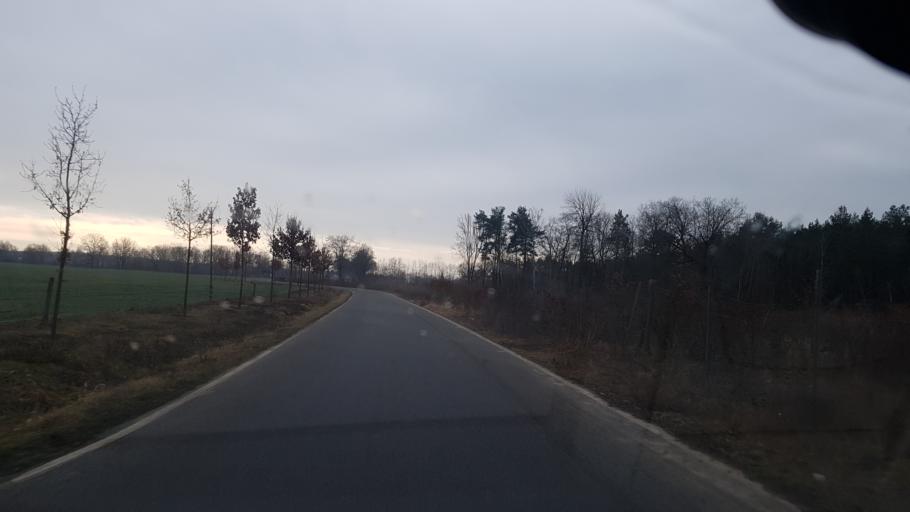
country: DE
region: Brandenburg
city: Cottbus
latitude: 51.7533
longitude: 14.4107
